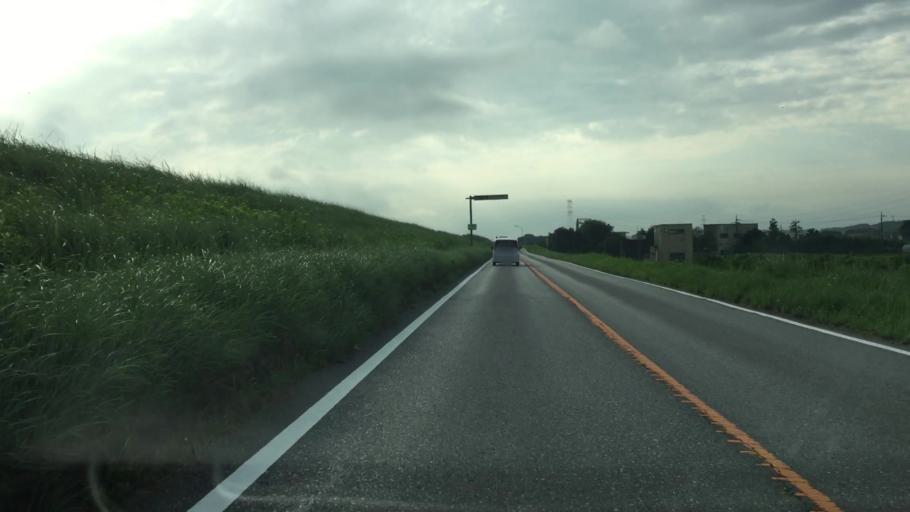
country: JP
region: Ibaraki
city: Toride
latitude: 35.8750
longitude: 140.1060
